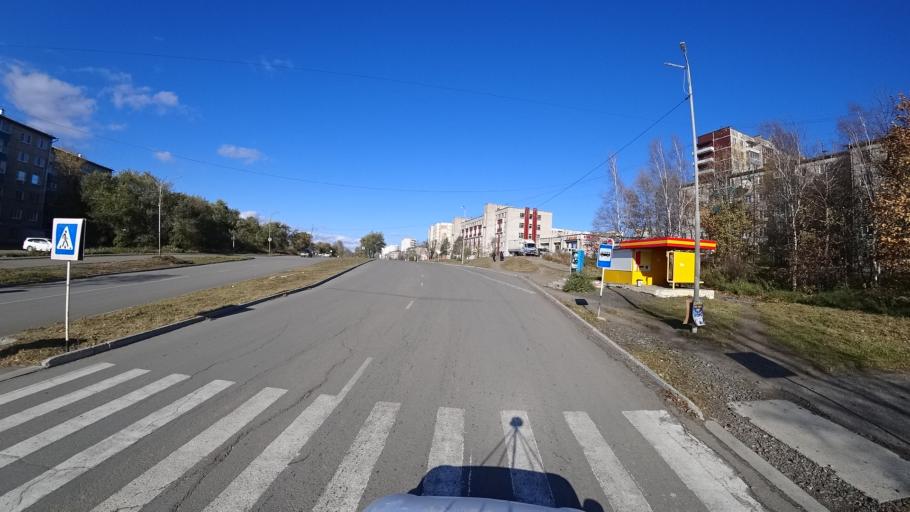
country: RU
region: Khabarovsk Krai
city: Amursk
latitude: 50.2418
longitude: 136.9137
